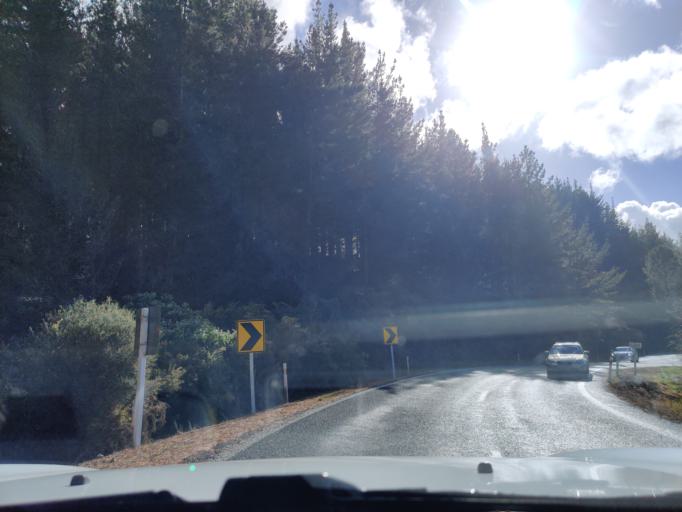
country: NZ
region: Waikato
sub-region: Thames-Coromandel District
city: Whitianga
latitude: -36.8868
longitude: 175.6741
